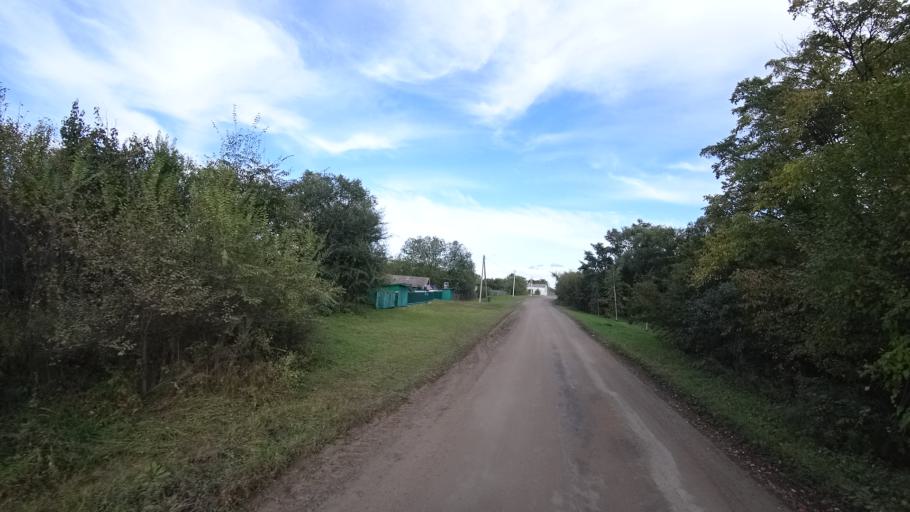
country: RU
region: Amur
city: Arkhara
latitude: 49.3568
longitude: 130.1139
